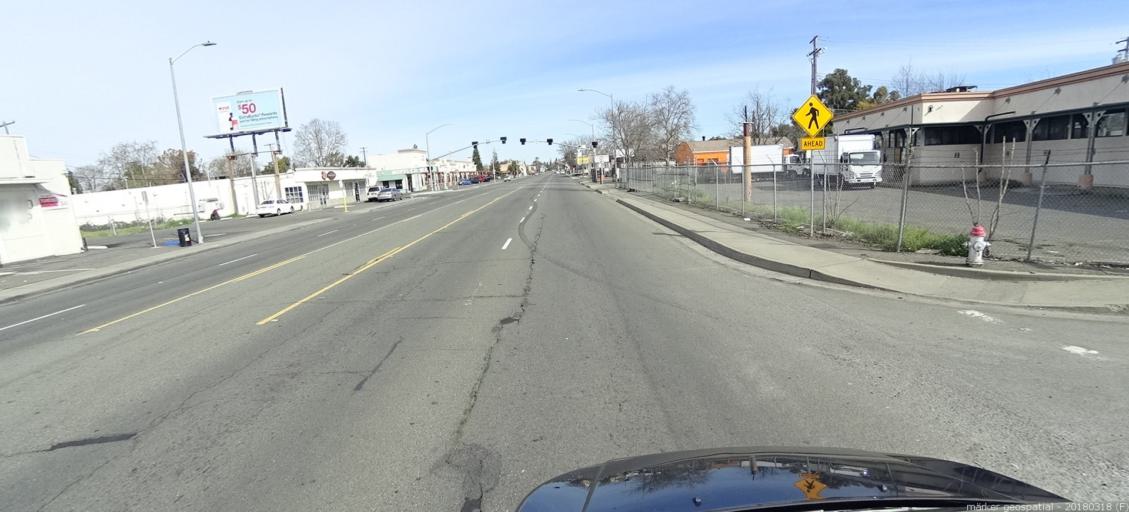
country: US
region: California
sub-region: Sacramento County
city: Parkway
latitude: 38.5308
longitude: -121.4732
